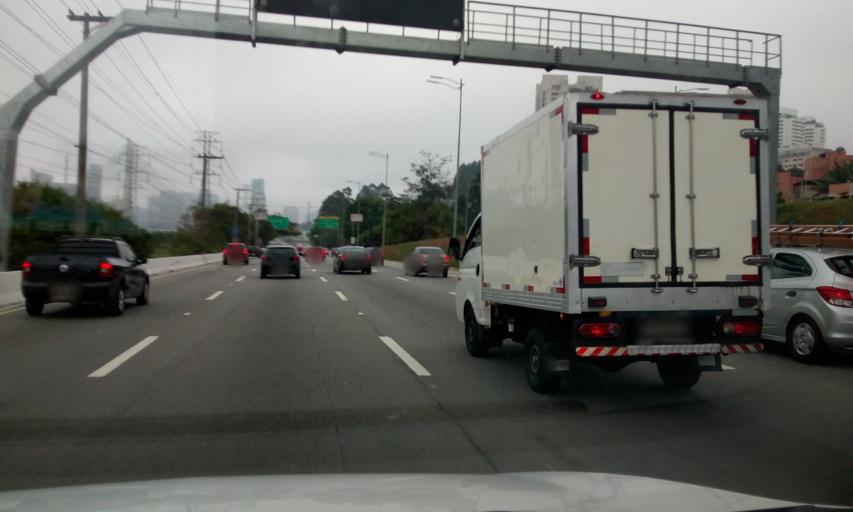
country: BR
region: Sao Paulo
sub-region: Sao Paulo
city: Sao Paulo
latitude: -23.6027
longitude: -46.6978
